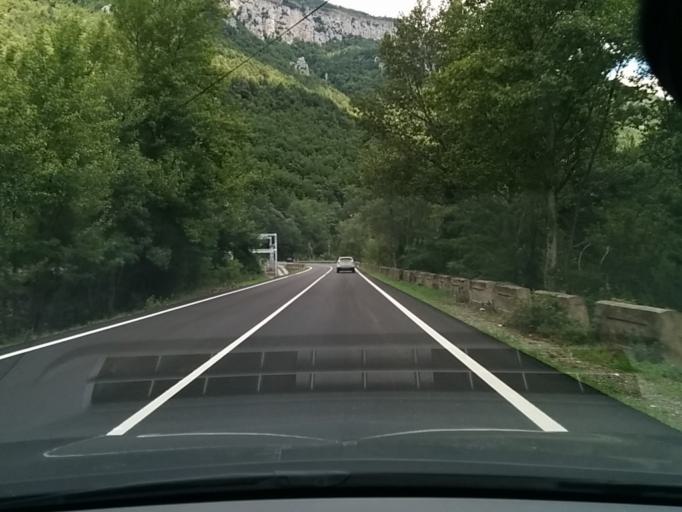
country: ES
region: Aragon
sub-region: Provincia de Huesca
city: Bielsa
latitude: 42.5804
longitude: 0.2024
